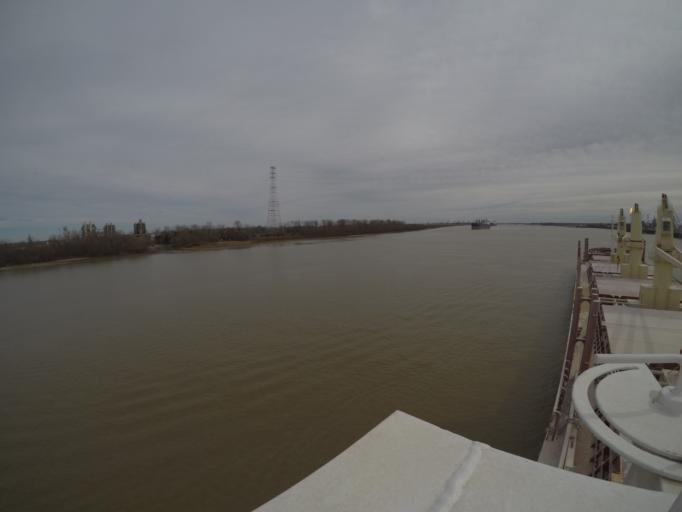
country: US
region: Louisiana
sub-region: Saint Charles Parish
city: Montz
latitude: 29.9983
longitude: -90.4649
